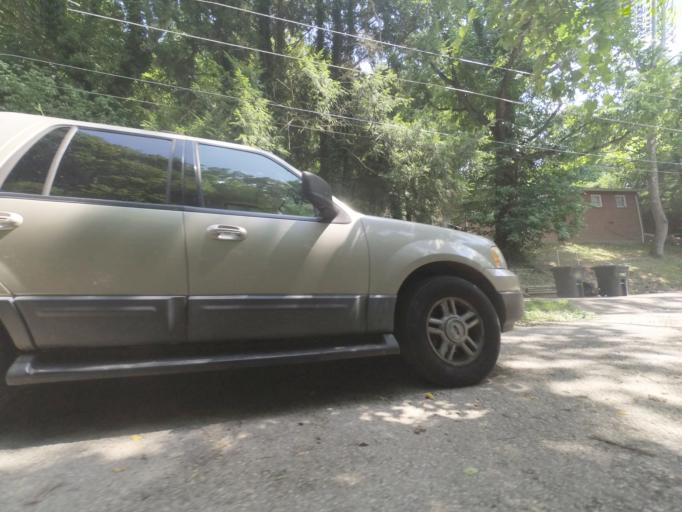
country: US
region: West Virginia
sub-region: Cabell County
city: Huntington
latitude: 38.3990
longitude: -82.4248
